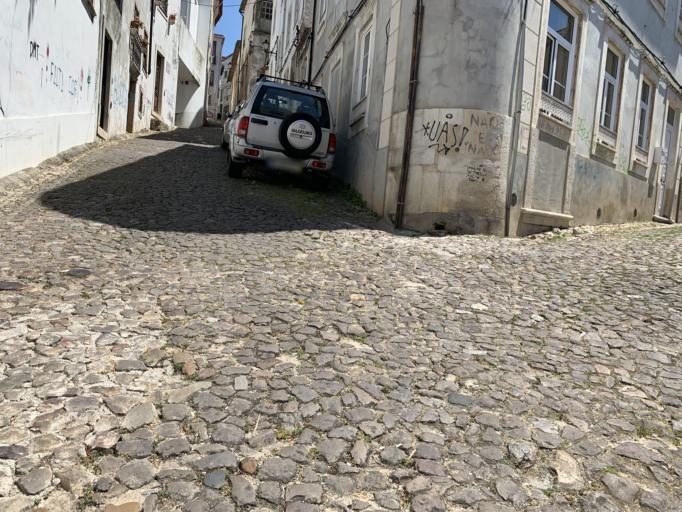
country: PT
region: Coimbra
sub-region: Coimbra
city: Coimbra
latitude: 40.2098
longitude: -8.4273
